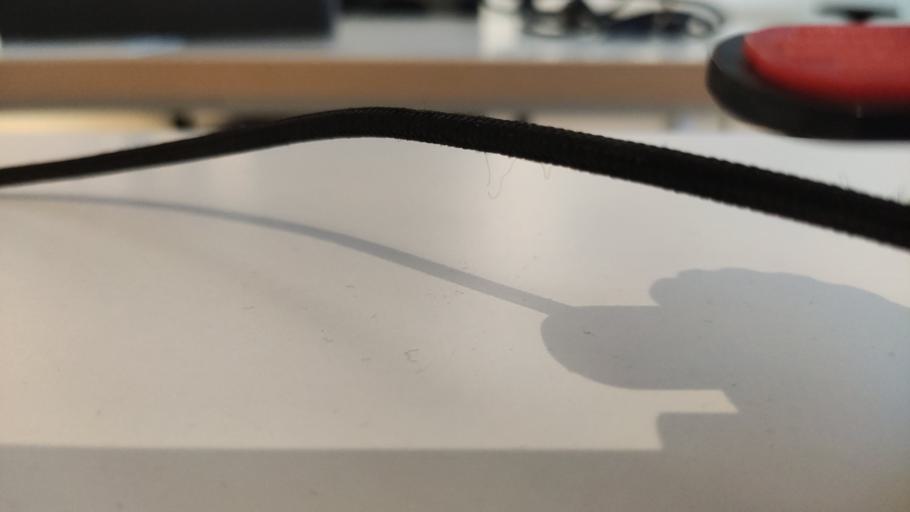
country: RU
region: Moskovskaya
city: Sychevo
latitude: 55.8433
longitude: 36.3375
